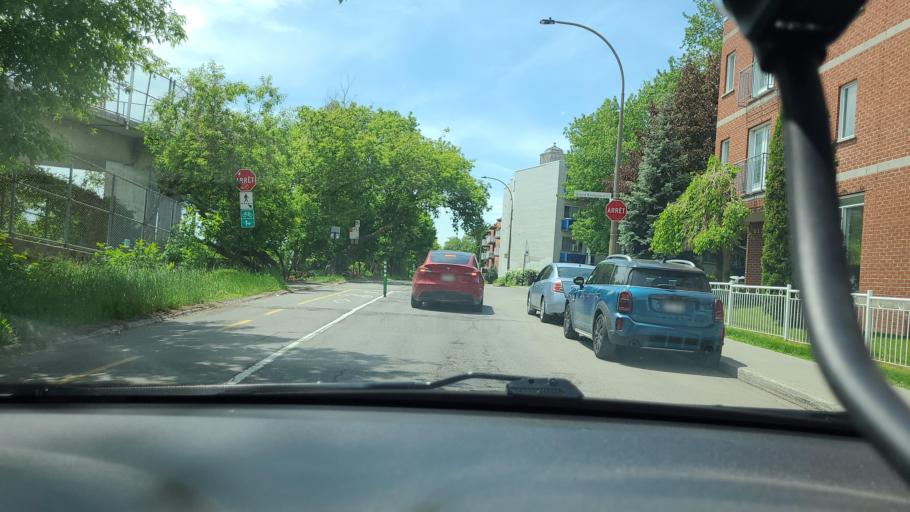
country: CA
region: Quebec
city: Saint-Raymond
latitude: 45.4654
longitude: -73.6197
